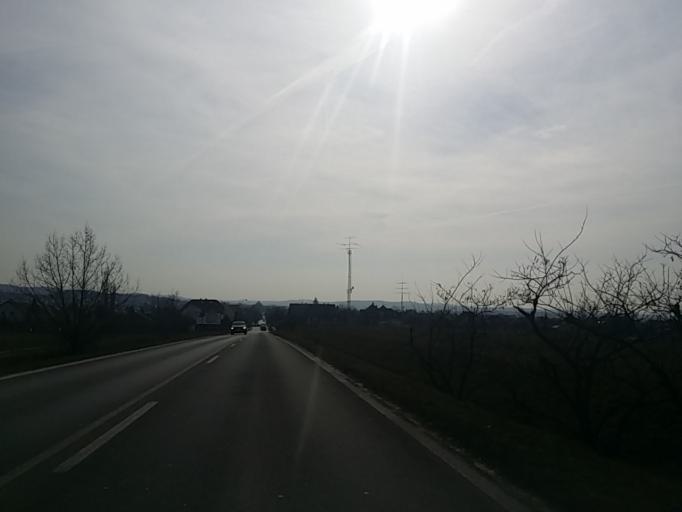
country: HU
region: Pest
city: Fot
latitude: 47.6336
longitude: 19.1726
